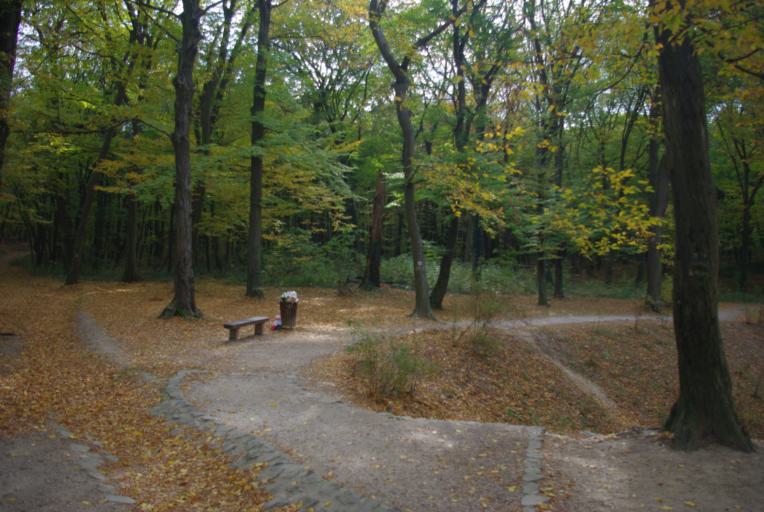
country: HU
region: Fejer
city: Bodajk
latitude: 47.3073
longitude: 18.2283
